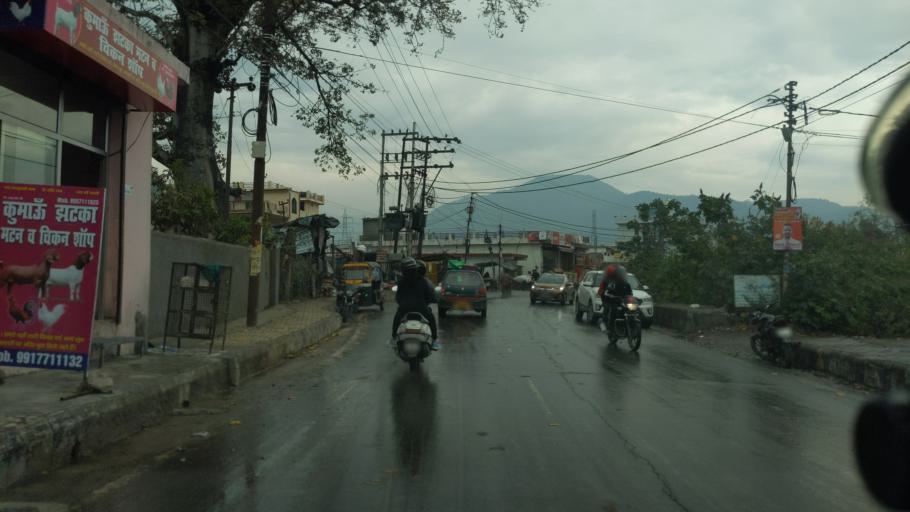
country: IN
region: Uttarakhand
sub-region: Naini Tal
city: Haldwani
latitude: 29.2436
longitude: 79.5307
